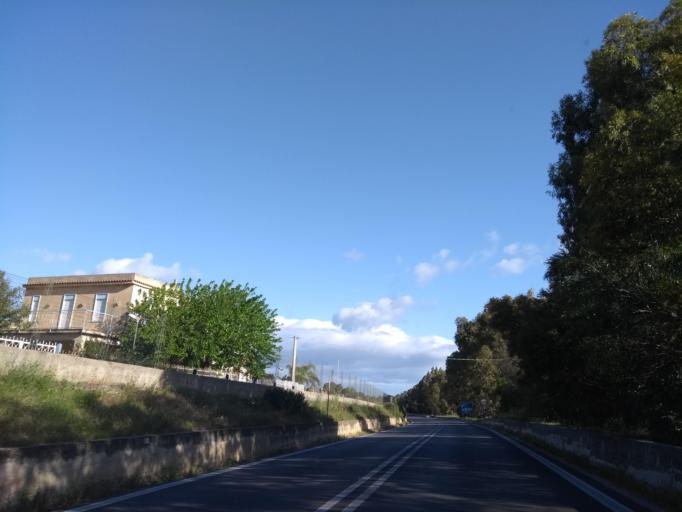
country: IT
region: Sicily
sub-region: Trapani
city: Alcamo
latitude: 38.0125
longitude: 12.9605
